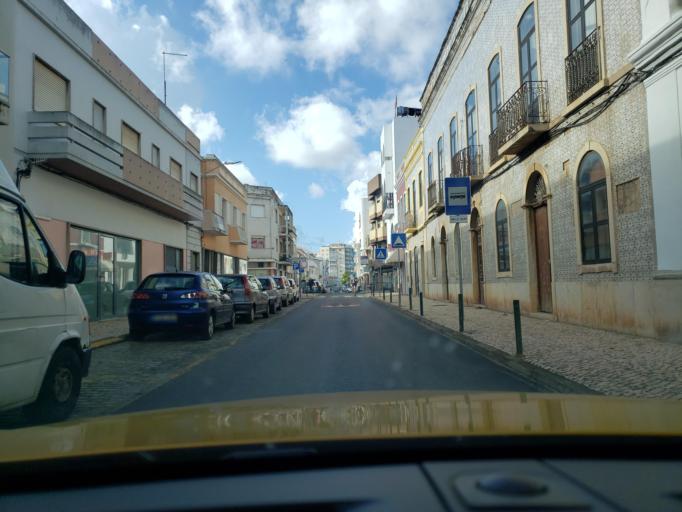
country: PT
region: Faro
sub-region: Portimao
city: Portimao
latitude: 37.1424
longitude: -8.5370
